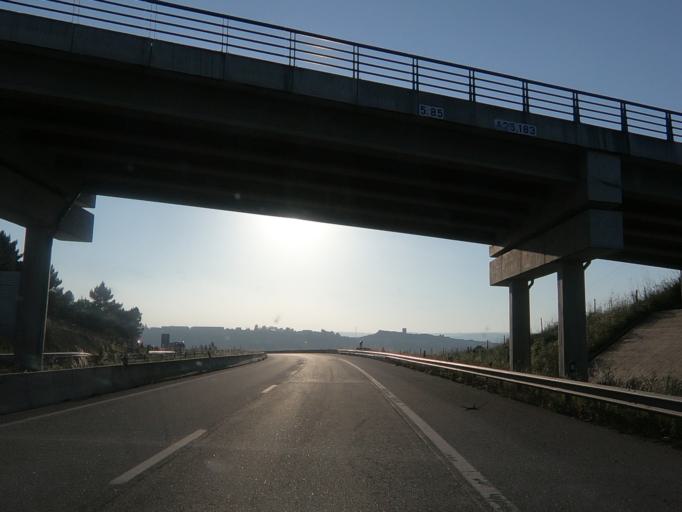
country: PT
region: Guarda
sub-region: Celorico da Beira
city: Celorico da Beira
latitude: 40.6274
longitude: -7.3702
